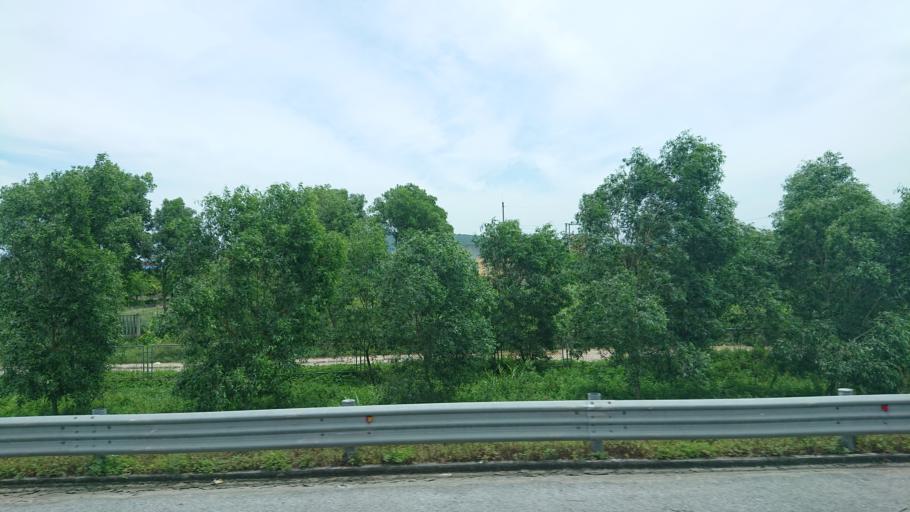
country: VN
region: Hai Phong
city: Nui Doi
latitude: 20.7707
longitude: 106.6154
